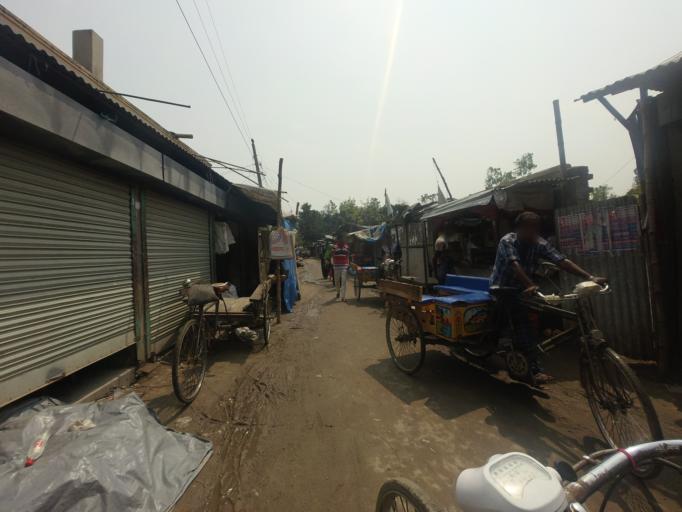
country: BD
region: Rajshahi
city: Sirajganj
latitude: 24.3641
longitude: 89.7199
